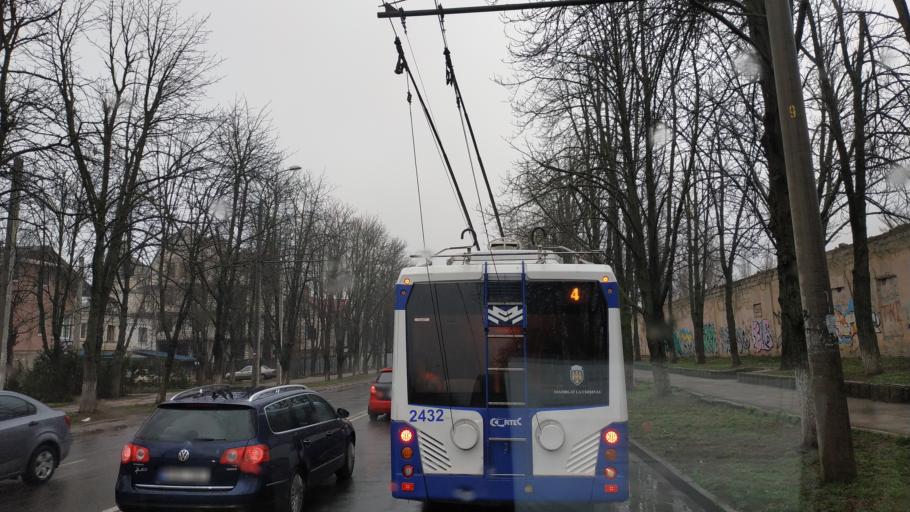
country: MD
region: Chisinau
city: Chisinau
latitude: 47.0234
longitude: 28.8035
